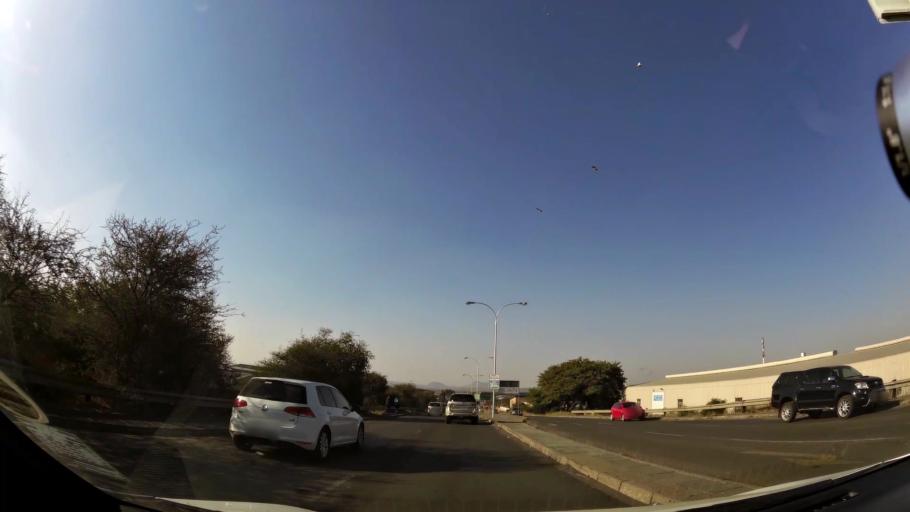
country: ZA
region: North-West
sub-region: Bojanala Platinum District Municipality
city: Rustenburg
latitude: -25.6697
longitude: 27.2560
